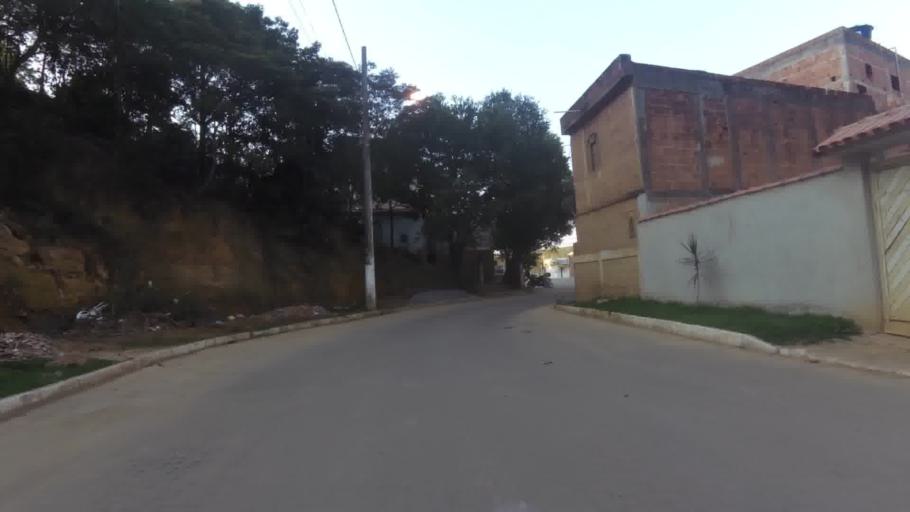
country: BR
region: Espirito Santo
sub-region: Piuma
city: Piuma
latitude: -20.8350
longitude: -40.7189
